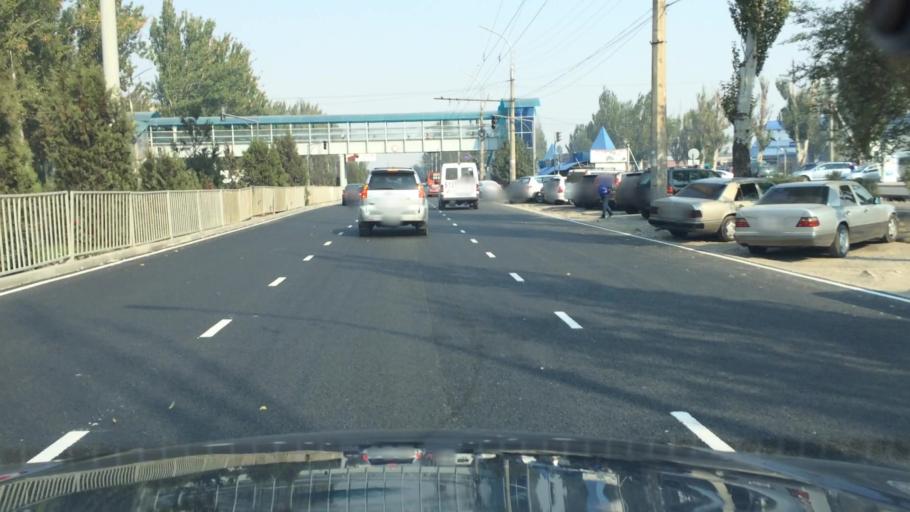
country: KG
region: Chuy
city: Lebedinovka
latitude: 42.8707
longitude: 74.6369
